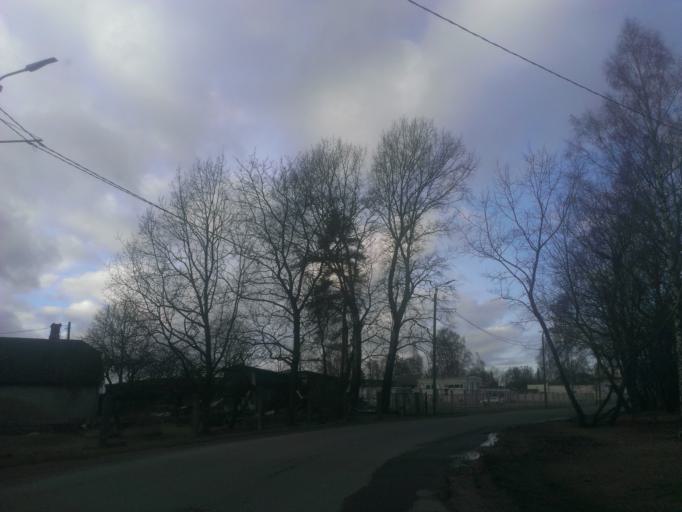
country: LV
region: Riga
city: Bolderaja
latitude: 57.0519
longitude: 24.0648
